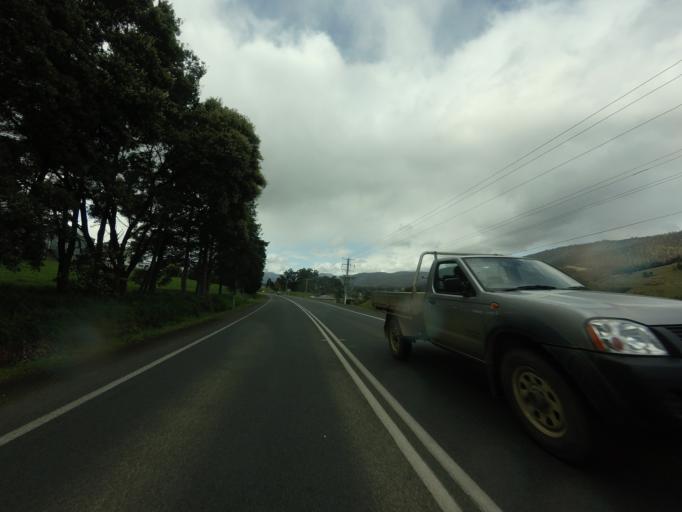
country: AU
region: Tasmania
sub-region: Huon Valley
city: Huonville
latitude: -43.0447
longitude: 147.0431
